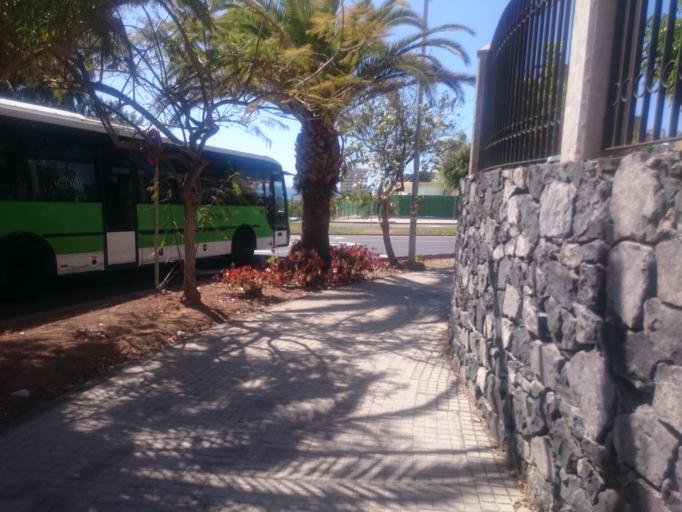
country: ES
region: Canary Islands
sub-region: Provincia de Santa Cruz de Tenerife
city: Playa de las Americas
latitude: 28.0515
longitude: -16.7084
